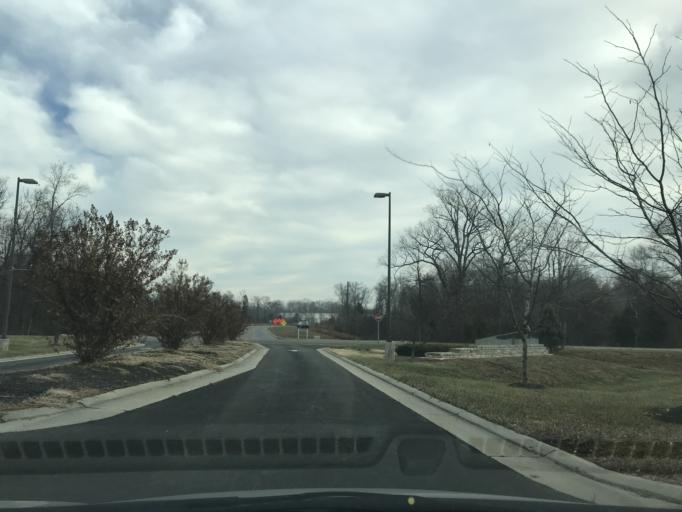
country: US
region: Virginia
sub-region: City of Manassas
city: Manassas
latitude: 38.7261
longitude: -77.5113
